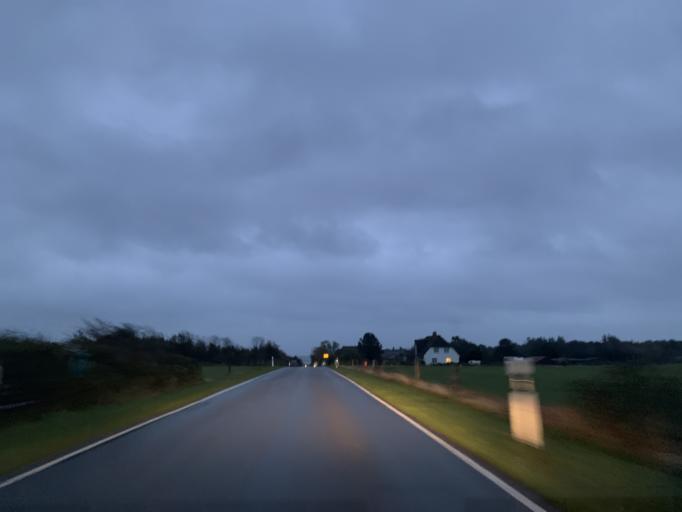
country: DE
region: Schleswig-Holstein
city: Wittdun
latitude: 54.6390
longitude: 8.3721
